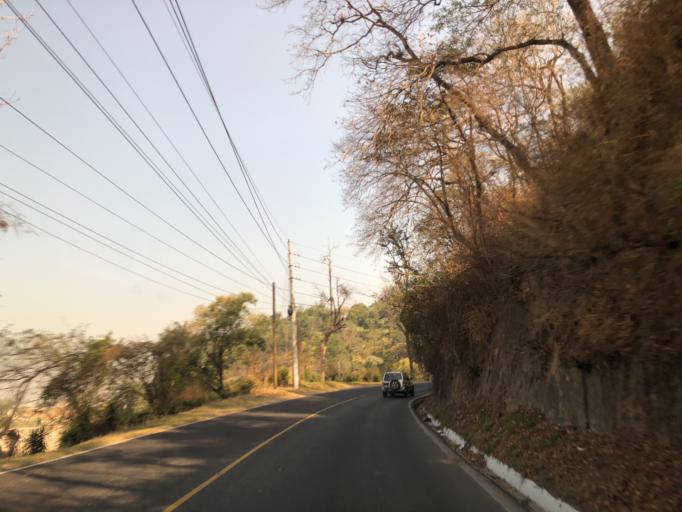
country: GT
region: Guatemala
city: Petapa
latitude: 14.4973
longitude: -90.5412
